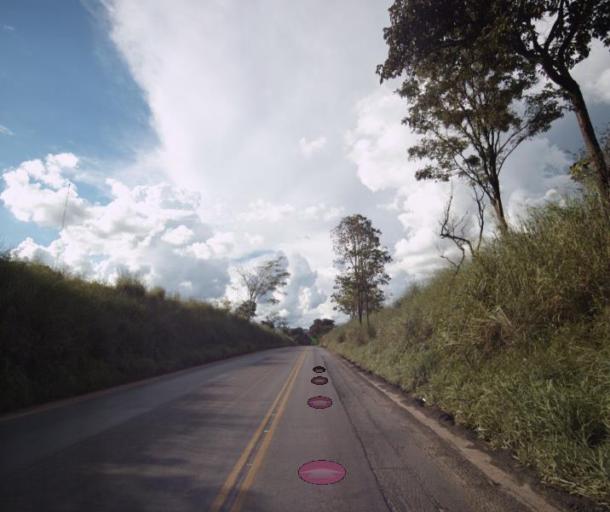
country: BR
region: Goias
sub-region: Rialma
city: Rialma
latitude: -15.3188
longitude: -49.5722
